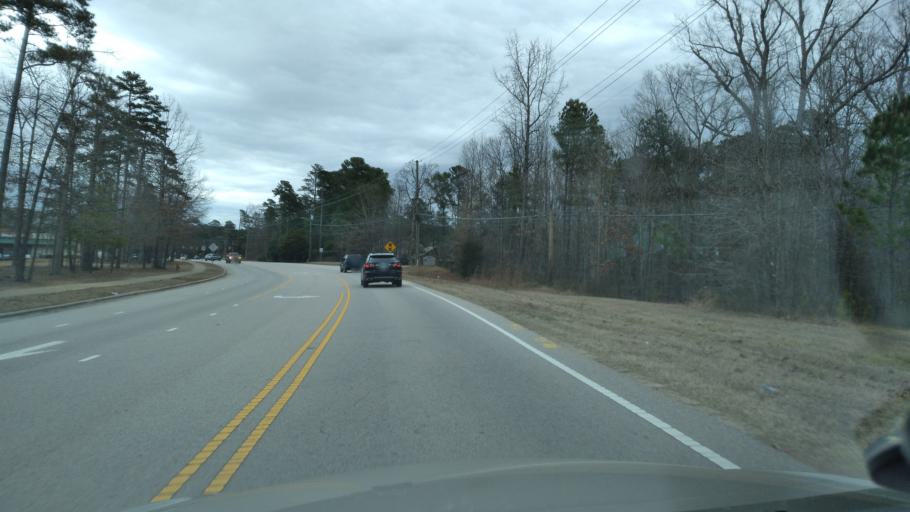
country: US
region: North Carolina
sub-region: Wake County
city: Apex
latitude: 35.7338
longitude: -78.8438
